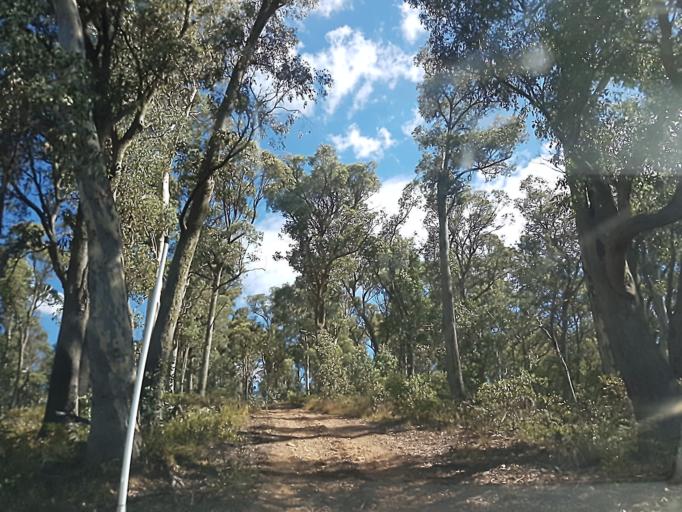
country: AU
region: Victoria
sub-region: Alpine
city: Mount Beauty
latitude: -36.8816
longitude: 147.0243
